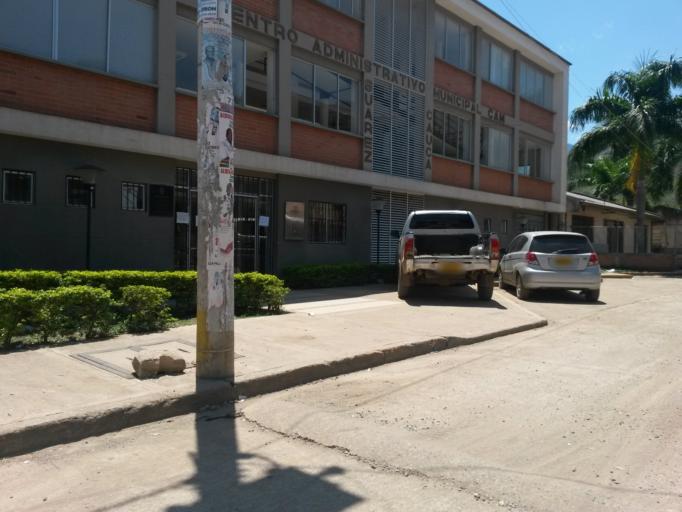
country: CO
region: Cauca
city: Suarez
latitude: 2.9521
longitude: -76.6938
